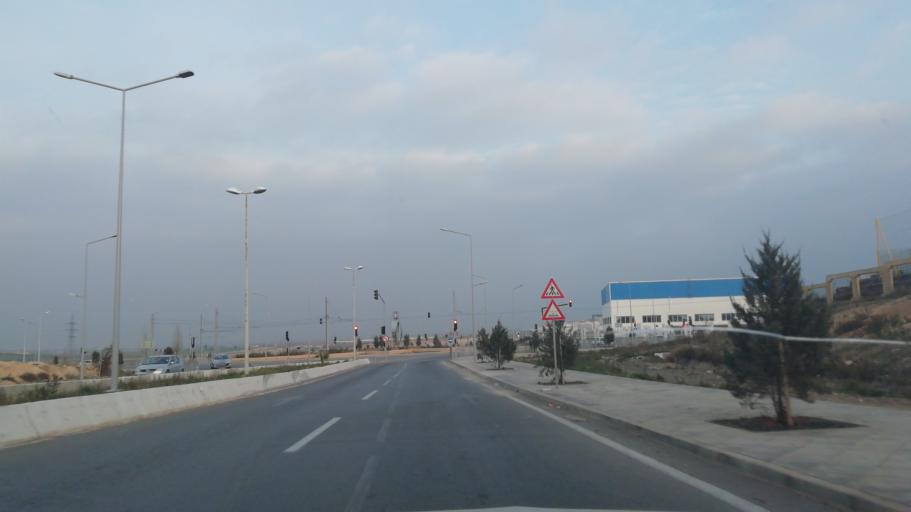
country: DZ
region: Sidi Bel Abbes
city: Sidi Bel Abbes
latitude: 35.2256
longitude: -0.6378
